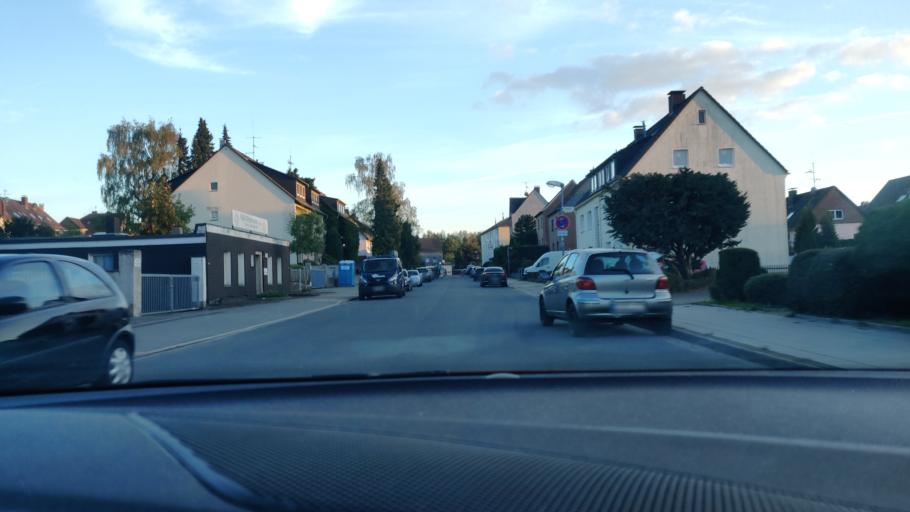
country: DE
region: North Rhine-Westphalia
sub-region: Regierungsbezirk Dusseldorf
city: Velbert
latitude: 51.3145
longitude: 7.0611
